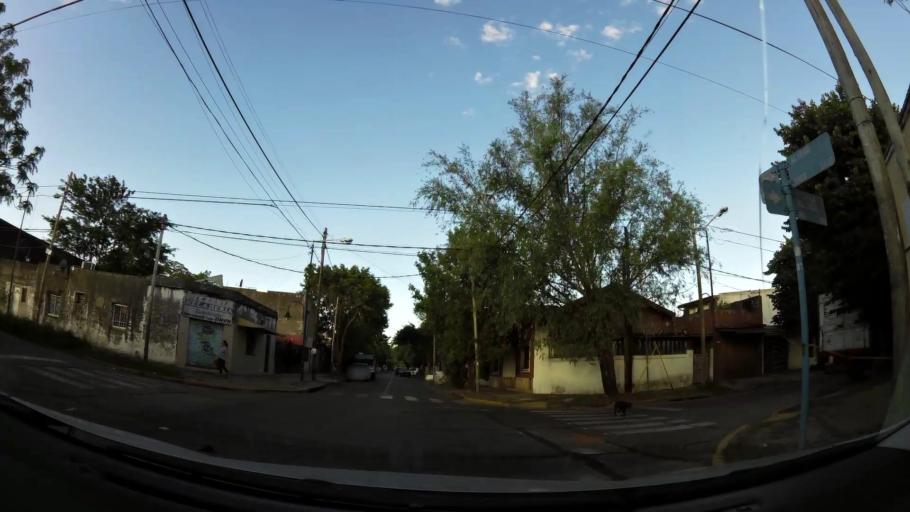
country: AR
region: Buenos Aires
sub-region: Partido de Tigre
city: Tigre
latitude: -34.4442
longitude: -58.5702
